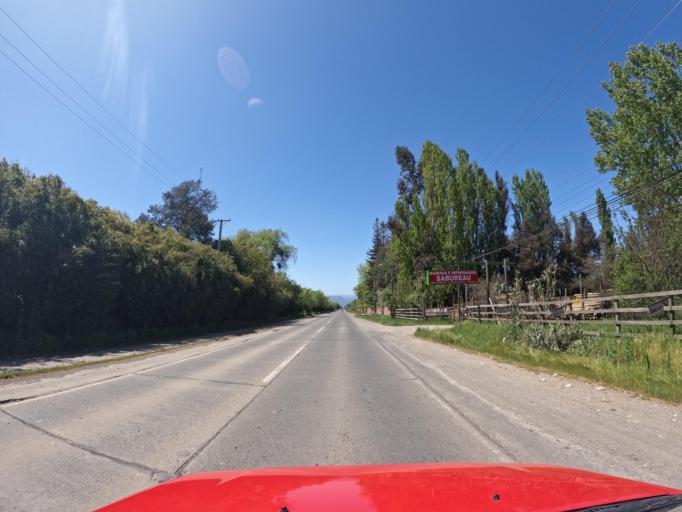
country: CL
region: Maule
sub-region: Provincia de Linares
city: Linares
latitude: -35.8338
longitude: -71.5401
